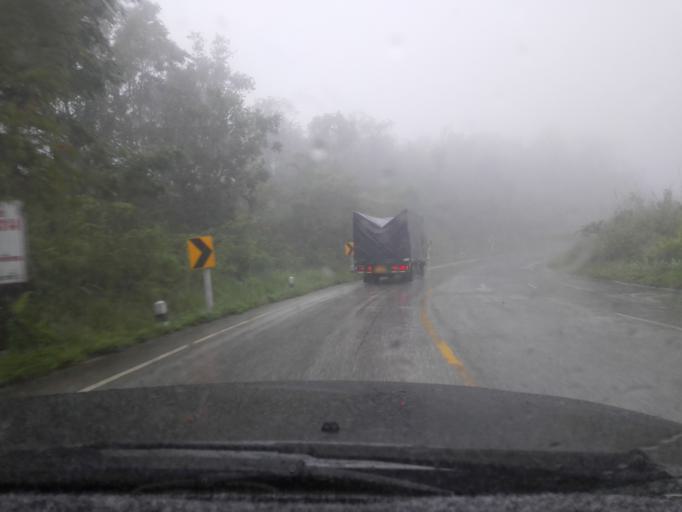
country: TH
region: Tak
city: Tak
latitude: 16.7635
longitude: 98.9027
